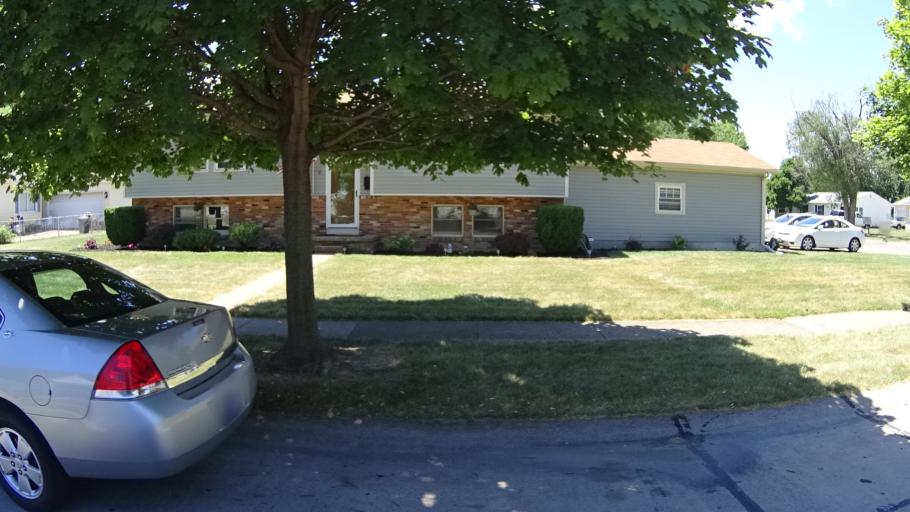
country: US
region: Ohio
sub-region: Erie County
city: Sandusky
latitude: 41.4387
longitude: -82.6884
